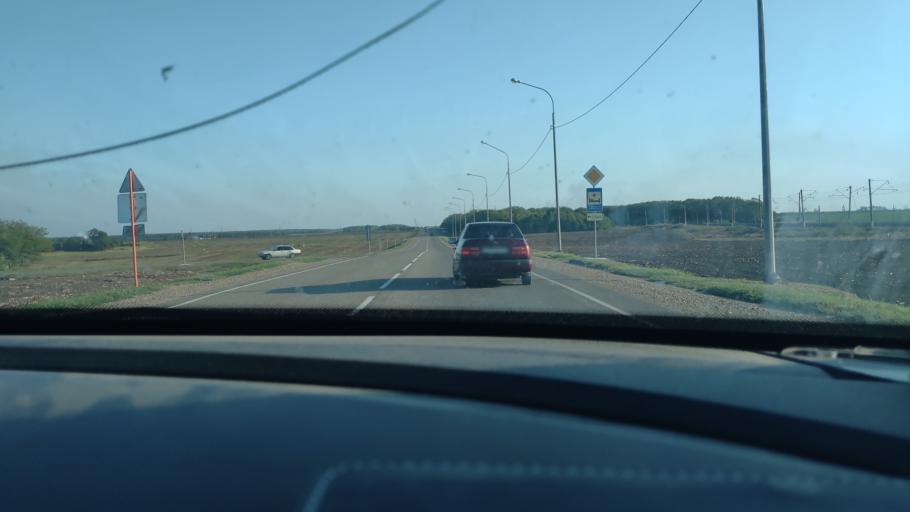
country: RU
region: Krasnodarskiy
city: Novominskaya
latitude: 46.3072
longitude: 38.9306
